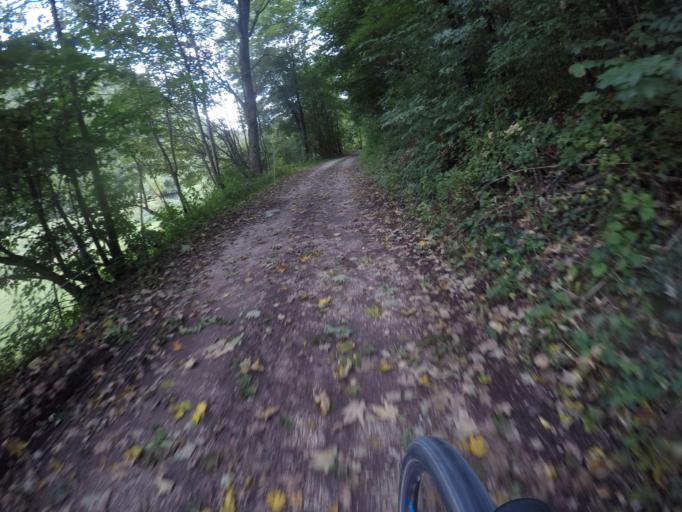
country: DE
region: Baden-Wuerttemberg
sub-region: Tuebingen Region
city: Bad Urach
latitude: 48.4649
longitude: 9.4222
